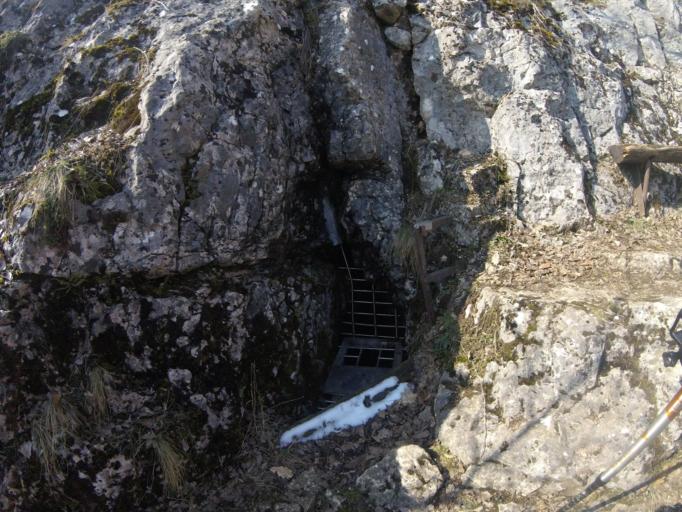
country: HU
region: Komarom-Esztergom
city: Nyergesujfalu
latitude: 47.7339
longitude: 18.5527
